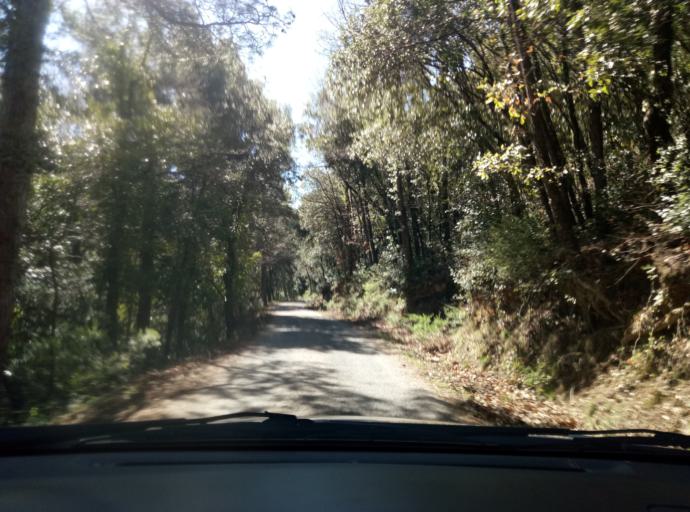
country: ES
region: Catalonia
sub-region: Provincia de Tarragona
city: Capafonts
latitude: 41.3408
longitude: 1.0567
